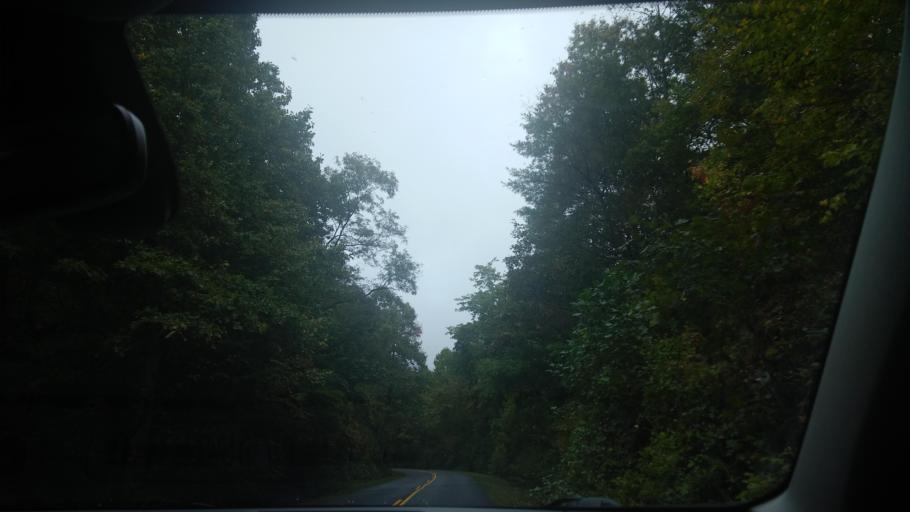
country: US
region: North Carolina
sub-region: Mitchell County
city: Spruce Pine
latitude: 35.9079
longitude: -81.9677
